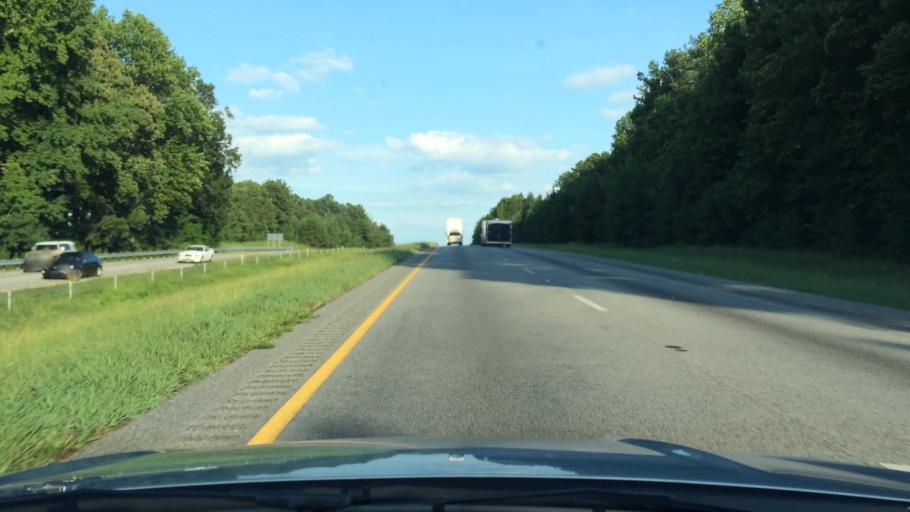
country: US
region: South Carolina
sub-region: Laurens County
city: Clinton
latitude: 34.4816
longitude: -81.8244
